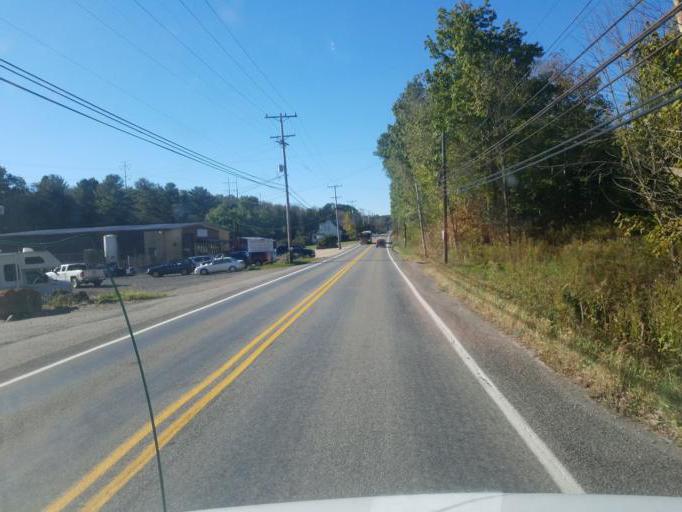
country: US
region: Pennsylvania
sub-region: Allegheny County
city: Imperial
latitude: 40.4623
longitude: -80.2664
